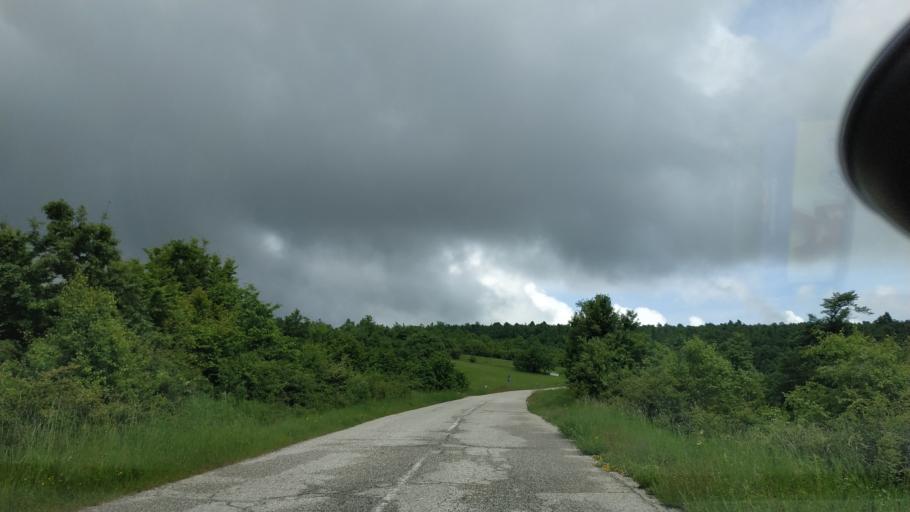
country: RS
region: Central Serbia
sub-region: Zajecarski Okrug
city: Soko Banja
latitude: 43.7197
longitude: 21.9459
